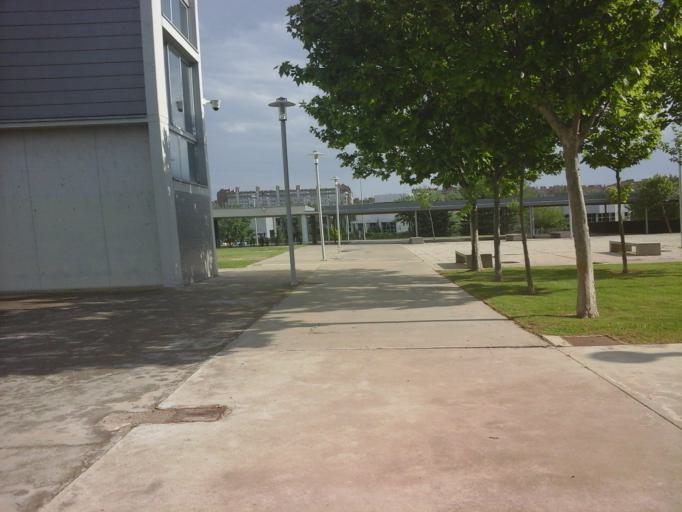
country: ES
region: Aragon
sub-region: Provincia de Zaragoza
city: Almozara
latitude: 41.6839
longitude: -0.8855
